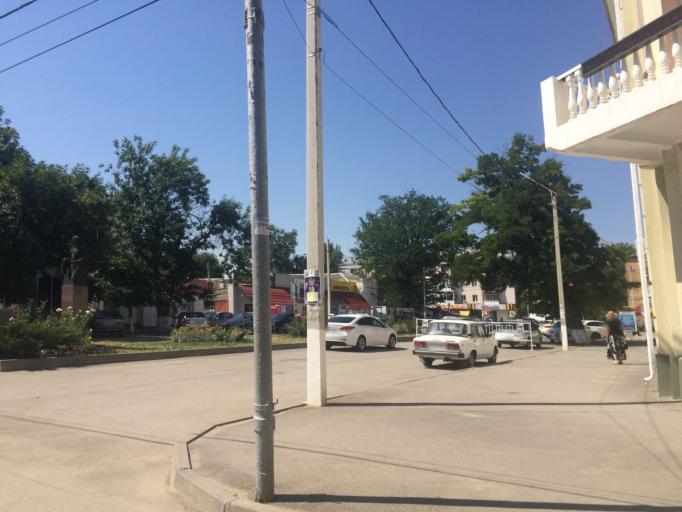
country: RU
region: Rostov
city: Sal'sk
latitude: 46.4728
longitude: 41.5436
